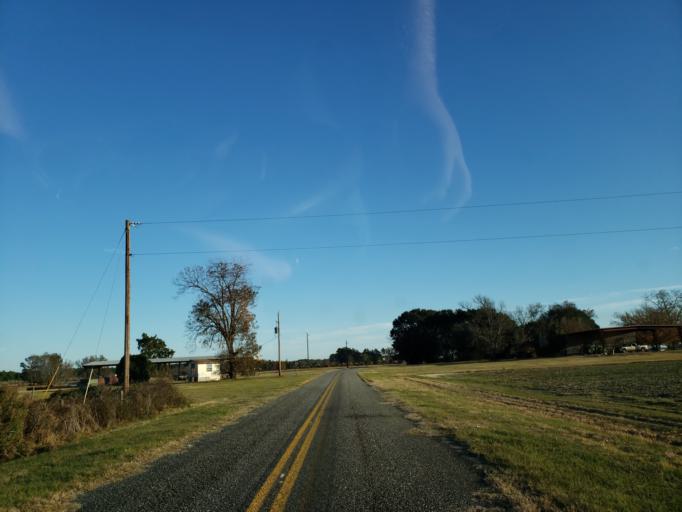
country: US
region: Georgia
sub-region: Dooly County
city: Unadilla
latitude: 32.1968
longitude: -83.7867
